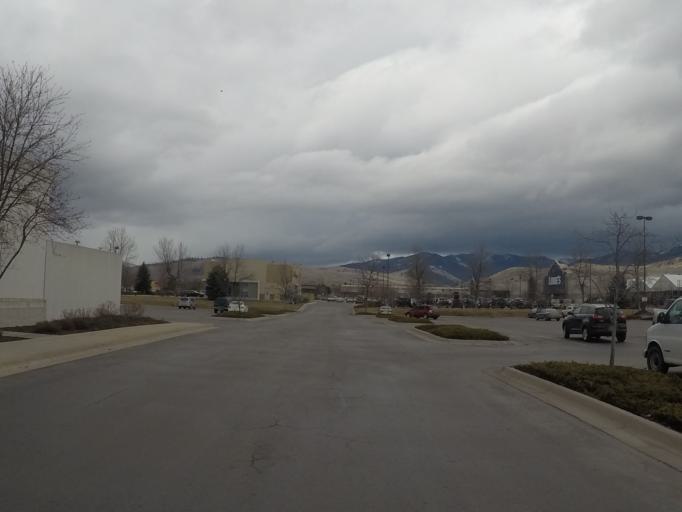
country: US
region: Montana
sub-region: Missoula County
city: Orchard Homes
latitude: 46.8911
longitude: -114.0382
